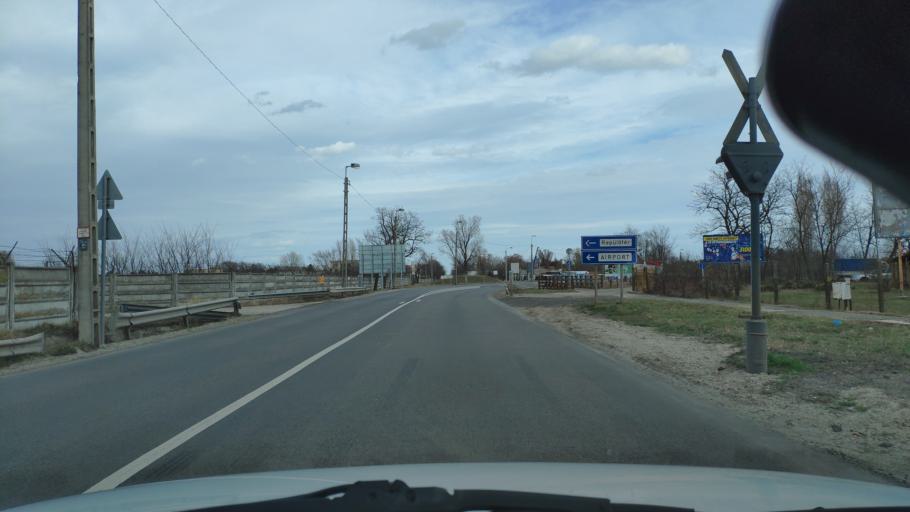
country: HU
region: Bacs-Kiskun
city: Kecskemet
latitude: 46.9083
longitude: 19.7408
